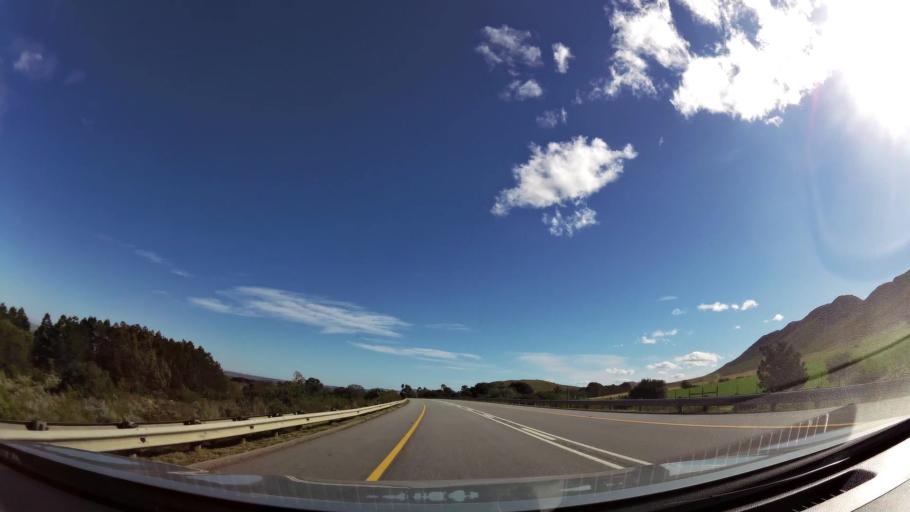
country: ZA
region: Eastern Cape
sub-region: Cacadu District Municipality
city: Kruisfontein
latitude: -33.9939
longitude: 24.6954
